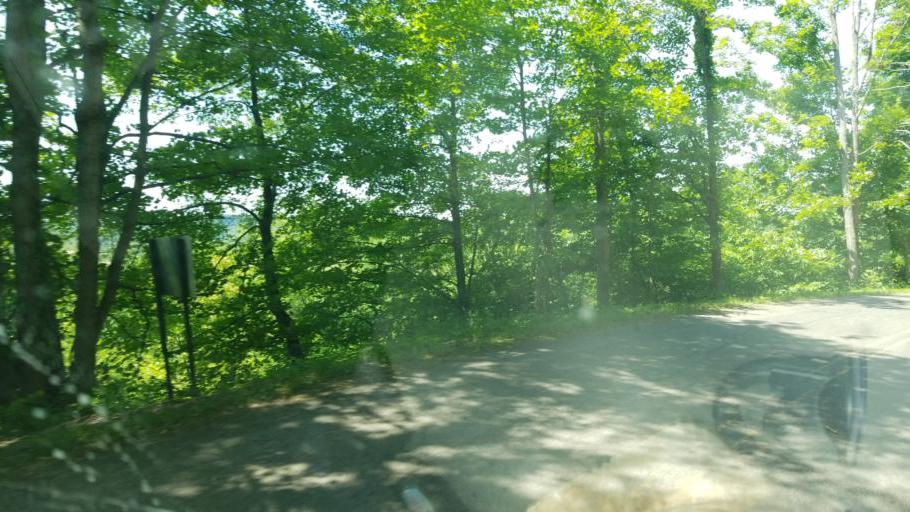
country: US
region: Ohio
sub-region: Knox County
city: Danville
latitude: 40.5098
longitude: -82.3630
